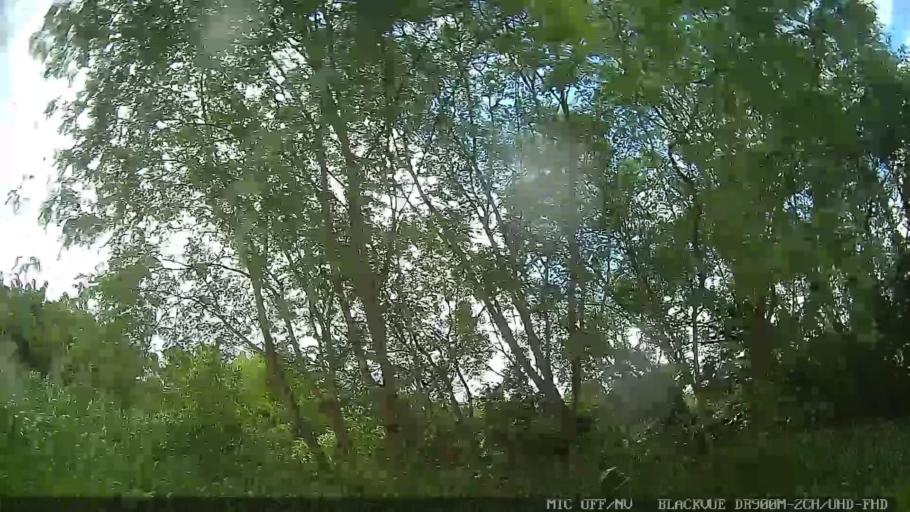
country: BR
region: Sao Paulo
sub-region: Jaguariuna
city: Jaguariuna
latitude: -22.6619
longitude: -47.0513
